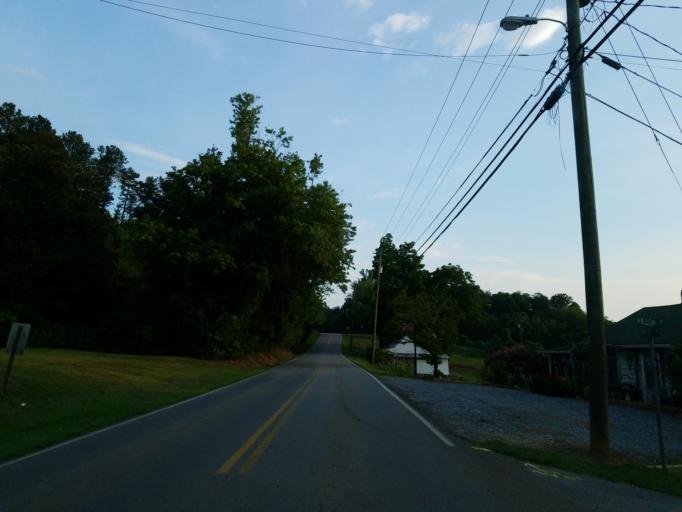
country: US
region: Georgia
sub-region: Gilmer County
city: Ellijay
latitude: 34.6829
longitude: -84.4734
